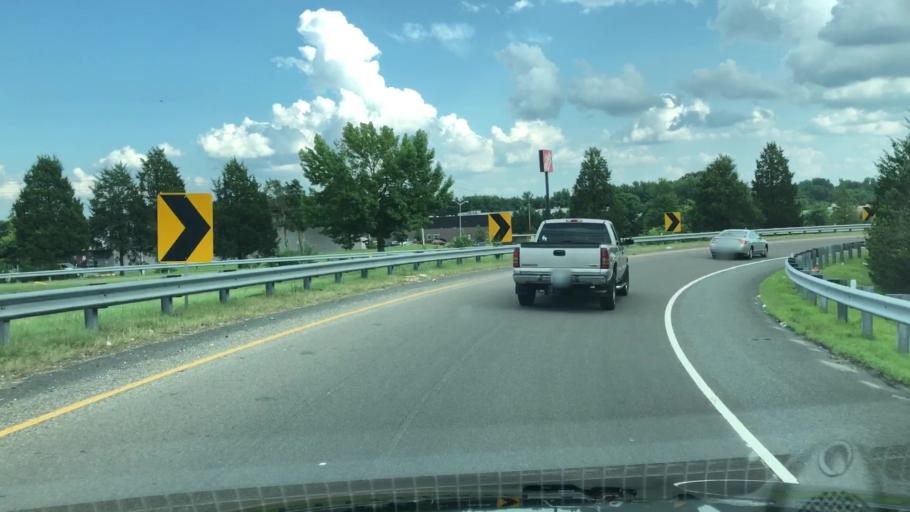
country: US
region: Virginia
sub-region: City of Fredericksburg
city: Fredericksburg
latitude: 38.2958
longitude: -77.5031
